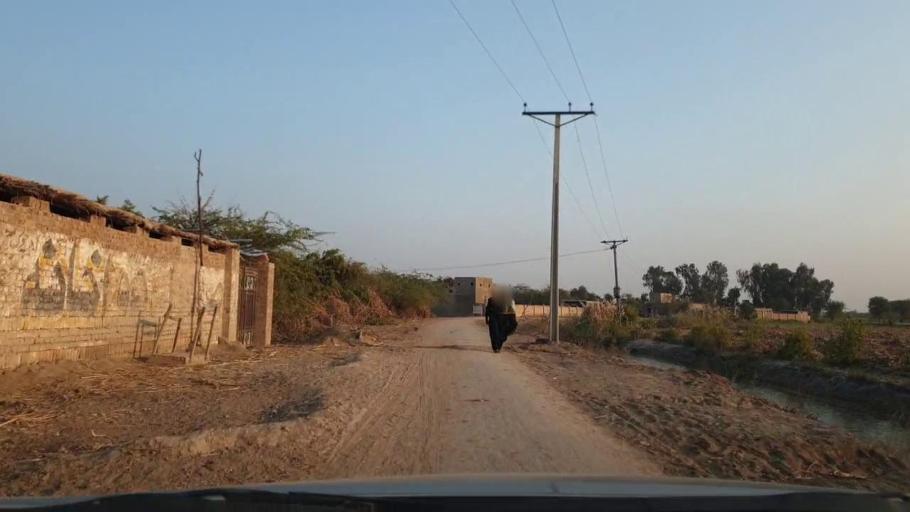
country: PK
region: Sindh
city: Tando Adam
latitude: 25.7133
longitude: 68.5850
